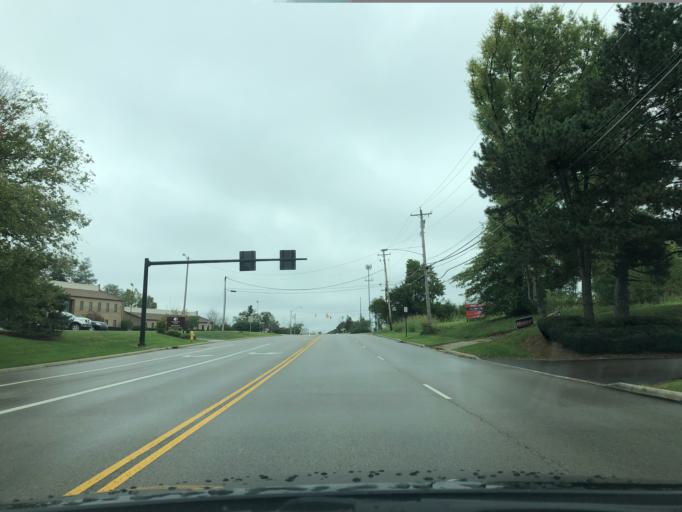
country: US
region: Ohio
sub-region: Hamilton County
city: Highpoint
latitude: 39.2829
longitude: -84.3706
